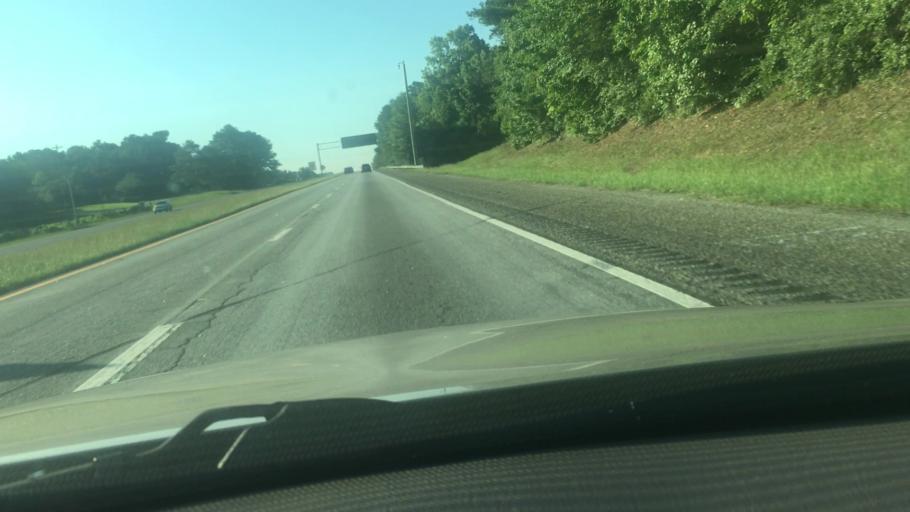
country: US
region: South Carolina
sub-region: Lexington County
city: Irmo
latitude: 34.1112
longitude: -81.1877
